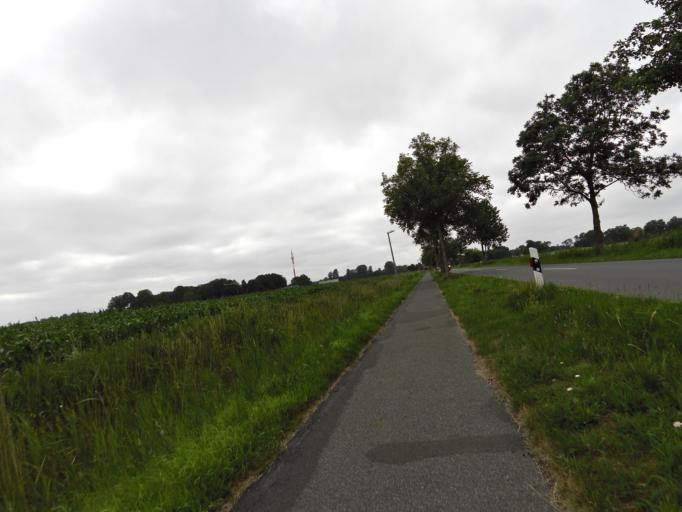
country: DE
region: Lower Saxony
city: Padingbuttel
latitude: 53.7214
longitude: 8.5439
